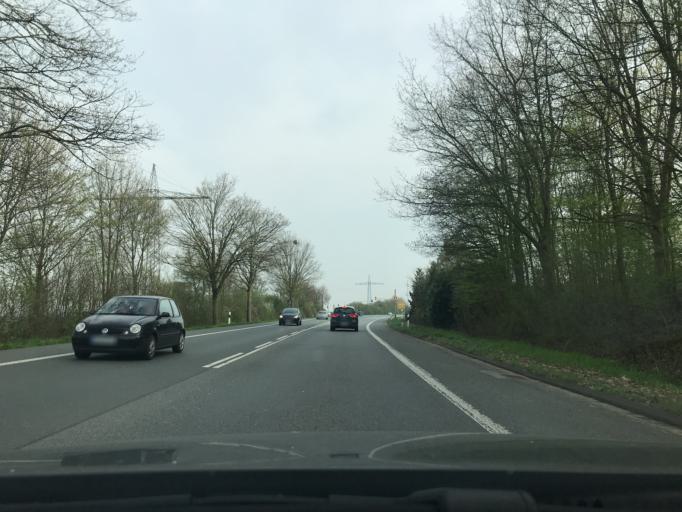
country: DE
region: North Rhine-Westphalia
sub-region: Regierungsbezirk Dusseldorf
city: Wachtendonk
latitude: 51.4610
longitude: 6.3784
